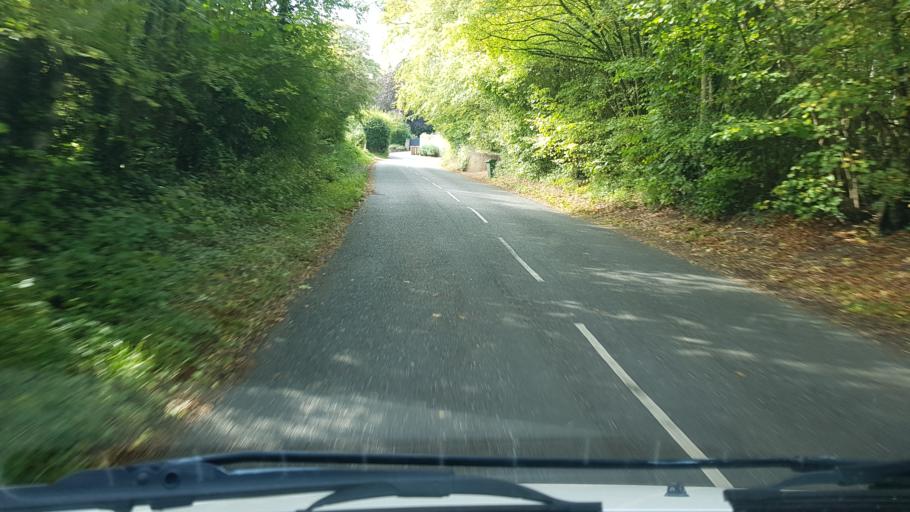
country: GB
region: England
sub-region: Surrey
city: Godalming
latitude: 51.2238
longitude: -0.6286
